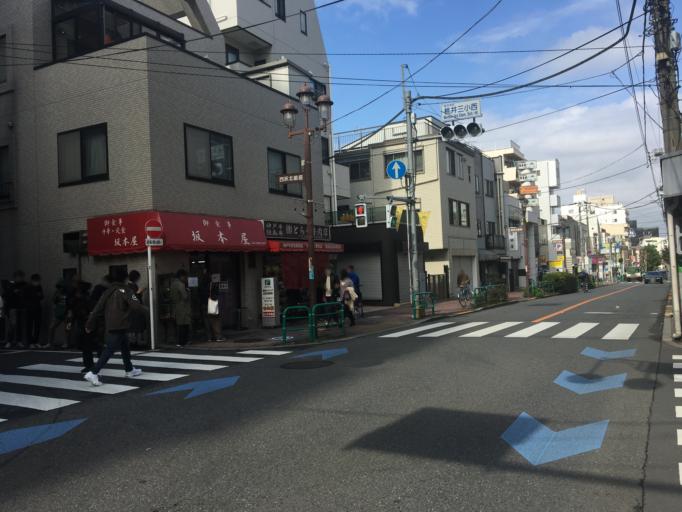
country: JP
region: Tokyo
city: Musashino
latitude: 35.7050
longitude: 139.6007
